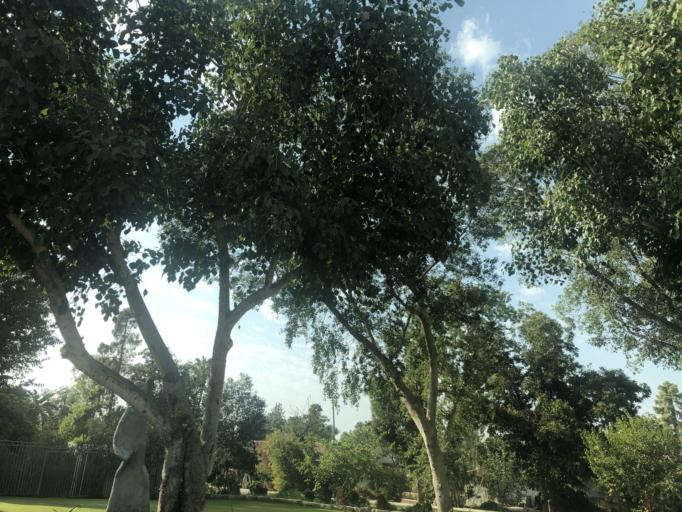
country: IL
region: Central District
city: Rosh Ha'Ayin
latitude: 32.0833
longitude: 34.9409
